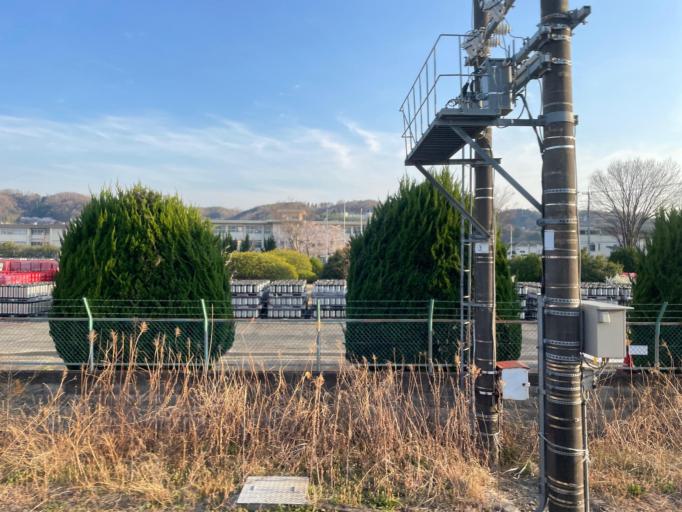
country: JP
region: Gunma
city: Annaka
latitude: 36.3376
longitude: 138.9508
